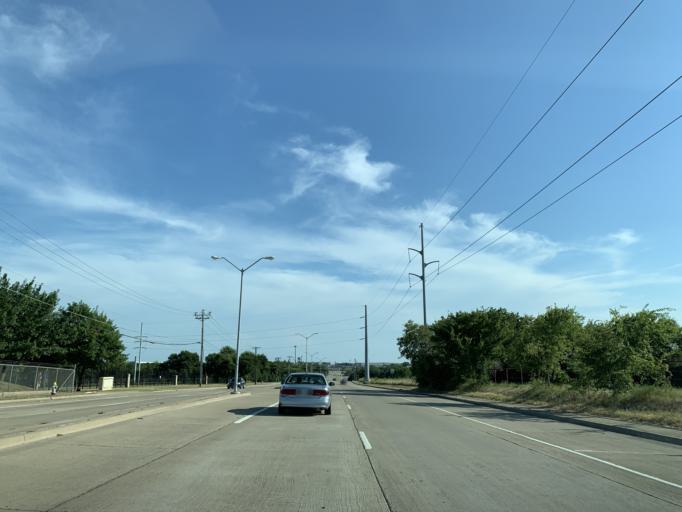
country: US
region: Texas
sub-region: Dallas County
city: Lancaster
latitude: 32.6544
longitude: -96.8058
